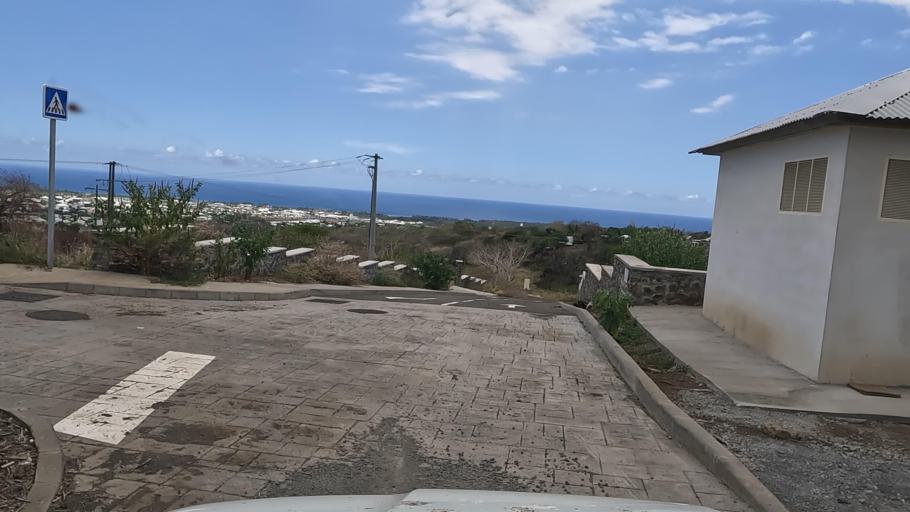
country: RE
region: Reunion
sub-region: Reunion
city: Saint-Louis
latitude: -21.2668
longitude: 55.4151
